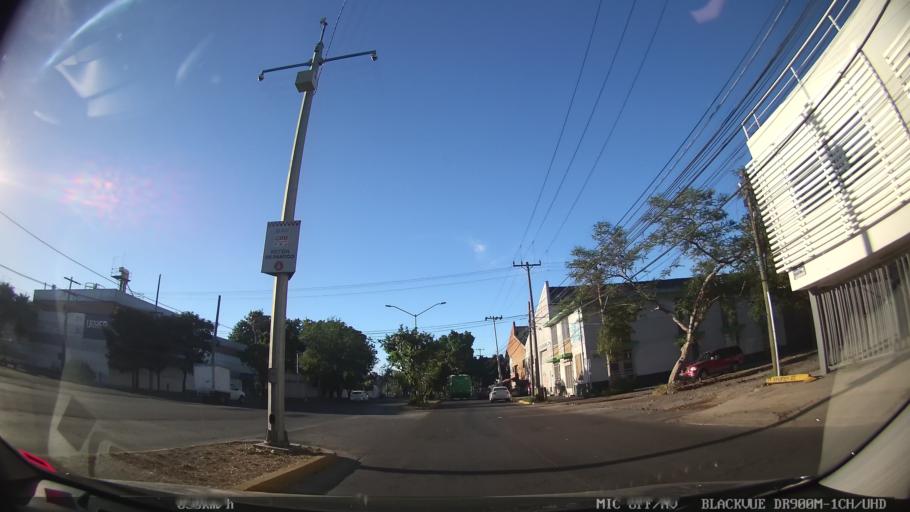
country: MX
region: Jalisco
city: Guadalajara
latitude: 20.6532
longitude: -103.3438
